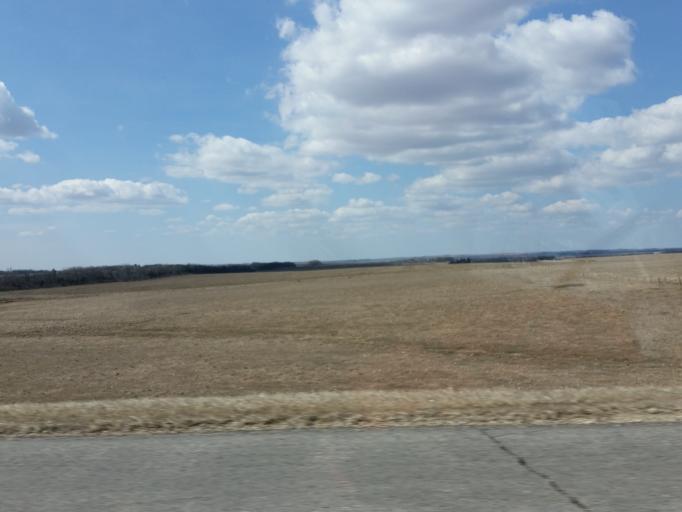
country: US
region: South Dakota
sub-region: Codington County
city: Watertown
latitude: 45.1905
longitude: -97.0570
